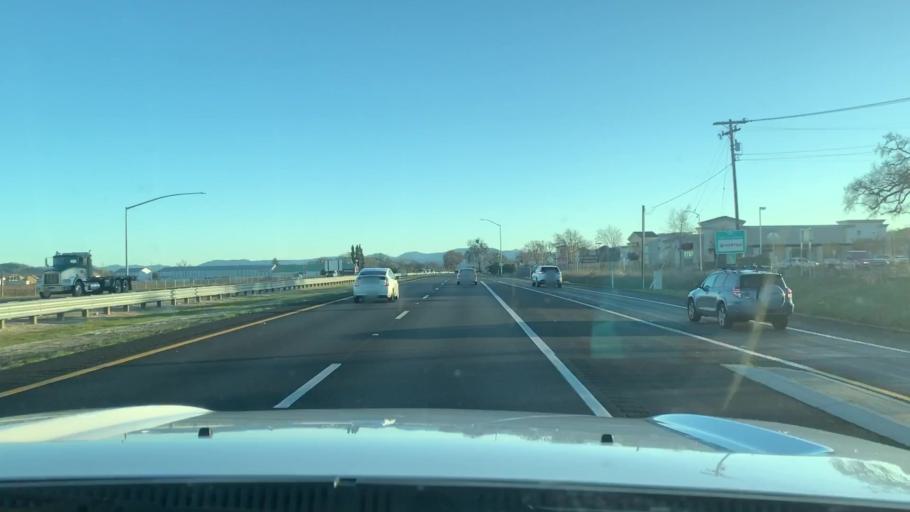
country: US
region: California
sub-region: San Luis Obispo County
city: Templeton
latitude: 35.5874
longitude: -120.6953
